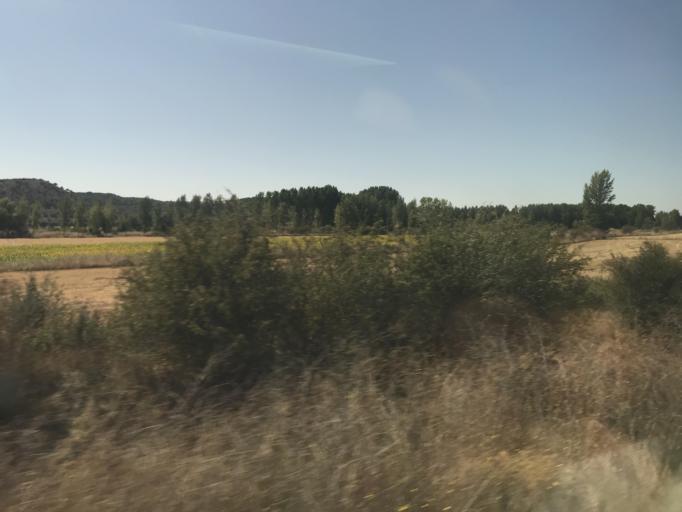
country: ES
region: Castille and Leon
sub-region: Provincia de Burgos
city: Villaldemiro
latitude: 42.2450
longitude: -3.9651
